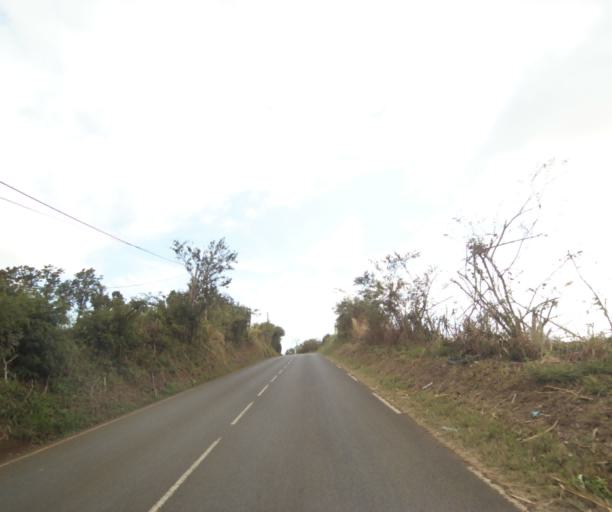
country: RE
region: Reunion
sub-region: Reunion
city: Trois-Bassins
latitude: -21.0670
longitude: 55.2783
